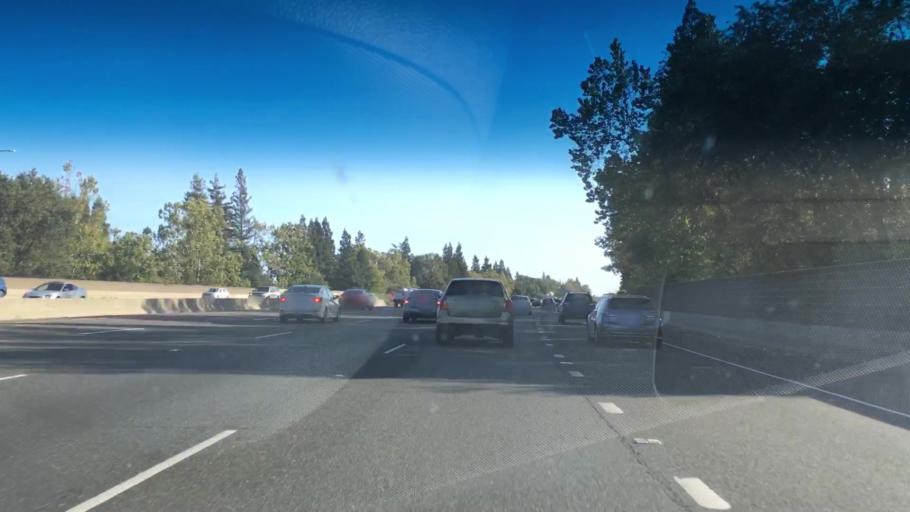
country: US
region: California
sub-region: Sacramento County
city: Parkway
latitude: 38.5027
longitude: -121.5182
